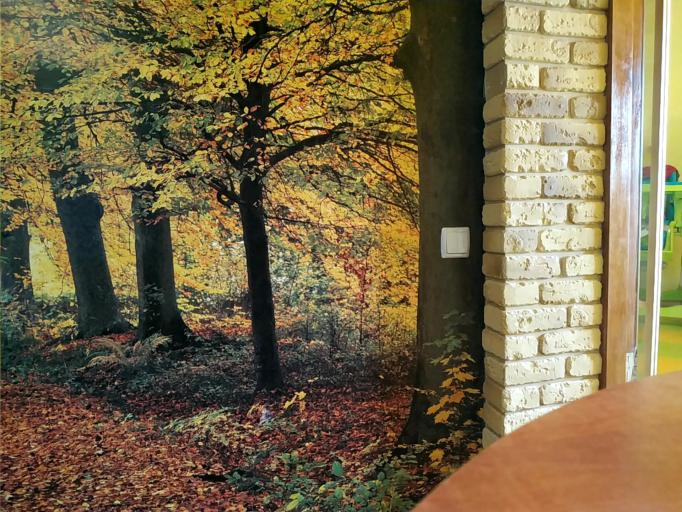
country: RU
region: Vologda
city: Nelazskoye
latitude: 59.4141
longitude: 37.6085
